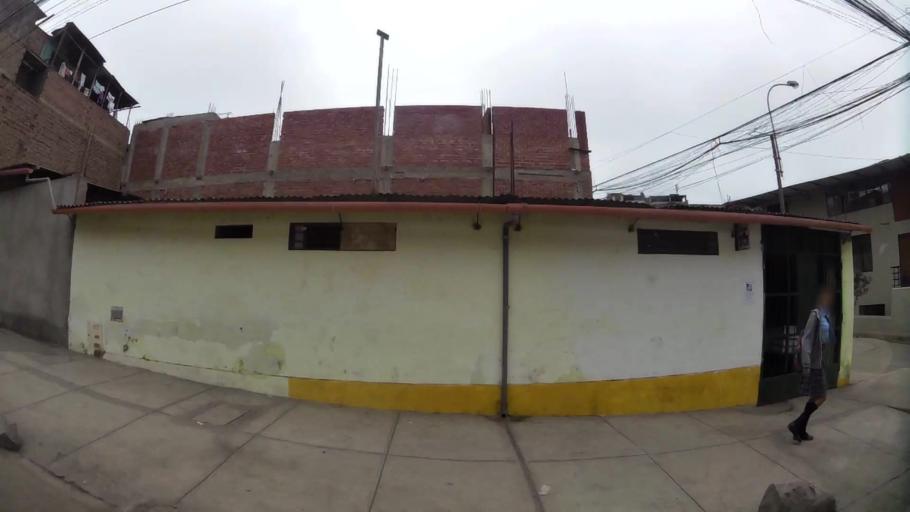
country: PE
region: Lima
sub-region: Lima
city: Surco
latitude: -12.1643
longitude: -76.9550
